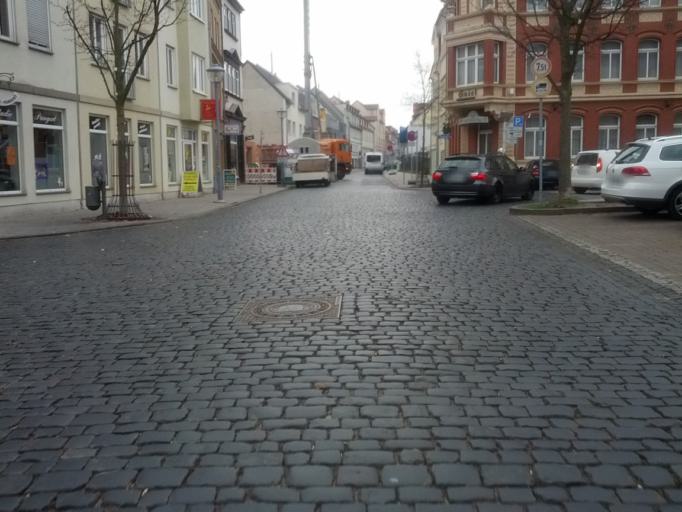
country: DE
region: Thuringia
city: Gotha
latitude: 50.9492
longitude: 10.7083
